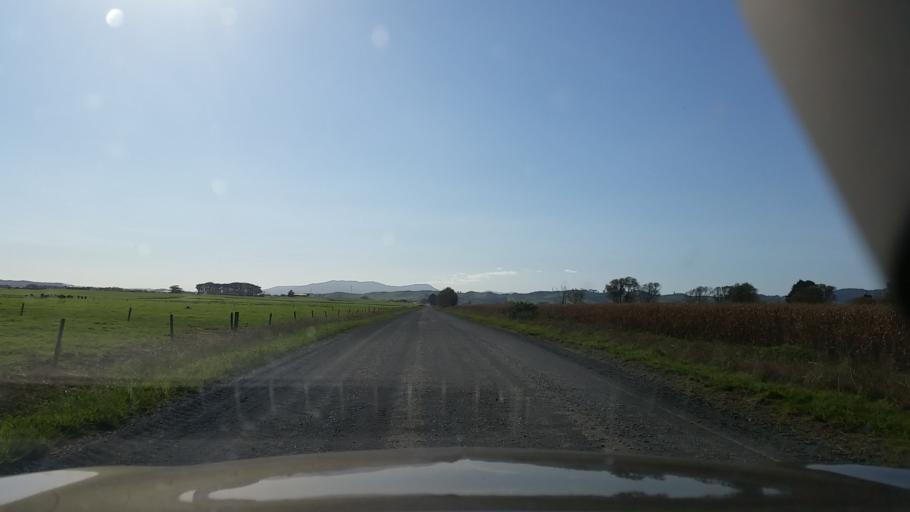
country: NZ
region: Waikato
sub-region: Hamilton City
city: Hamilton
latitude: -37.6329
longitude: 175.4289
